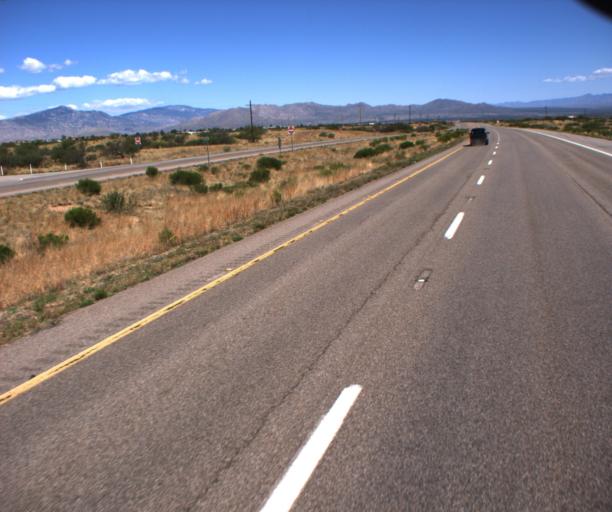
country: US
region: Arizona
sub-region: Cochise County
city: Whetstone
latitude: 31.9439
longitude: -110.3410
